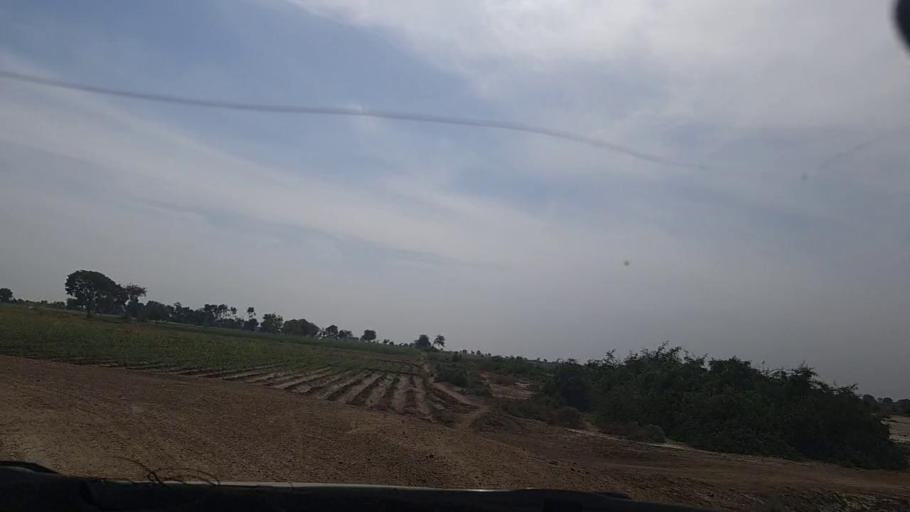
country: PK
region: Sindh
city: Pithoro
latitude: 25.4551
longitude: 69.4696
